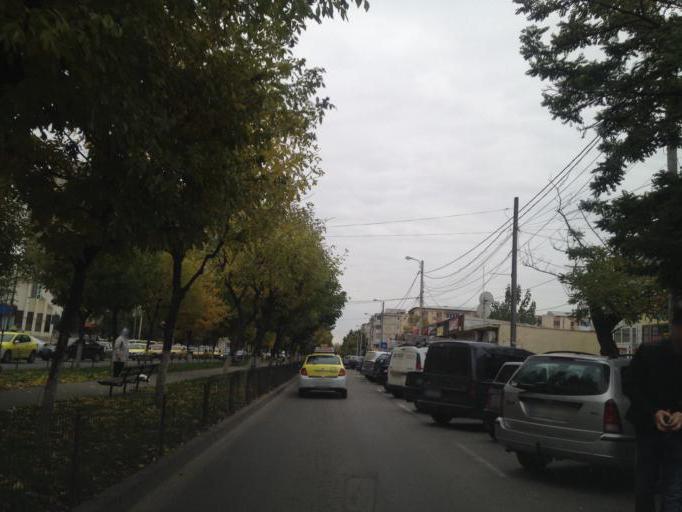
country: RO
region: Dolj
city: Craiova
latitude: 44.3366
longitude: 23.7769
